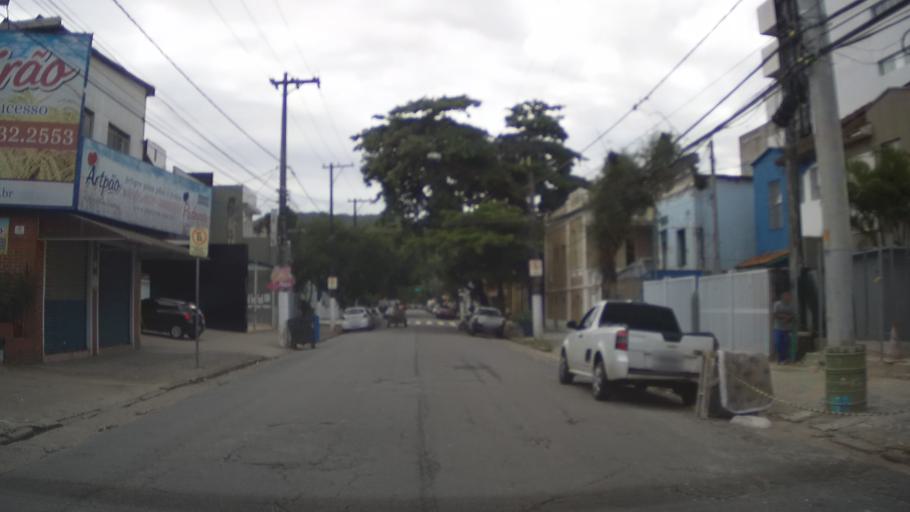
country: BR
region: Sao Paulo
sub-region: Santos
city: Santos
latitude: -23.9491
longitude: -46.3322
